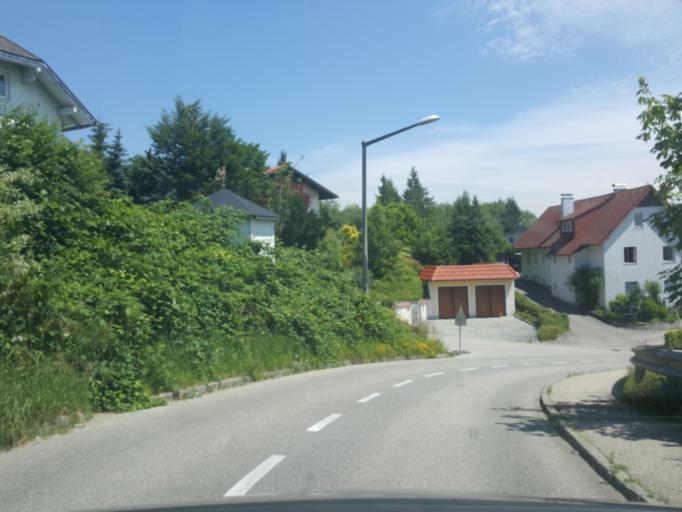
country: AT
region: Upper Austria
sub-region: Politischer Bezirk Vocklabruck
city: Seewalchen
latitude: 47.9566
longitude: 13.5806
